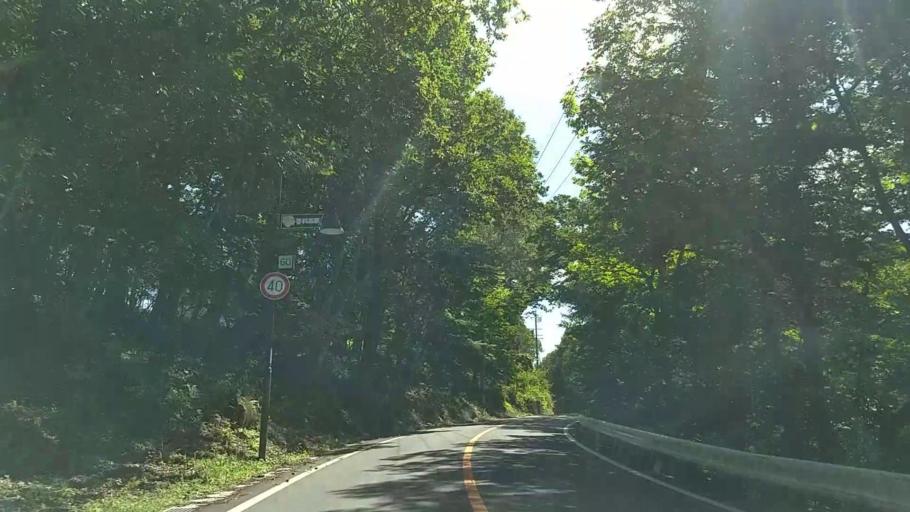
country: JP
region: Nagano
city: Chino
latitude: 36.0555
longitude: 138.2689
